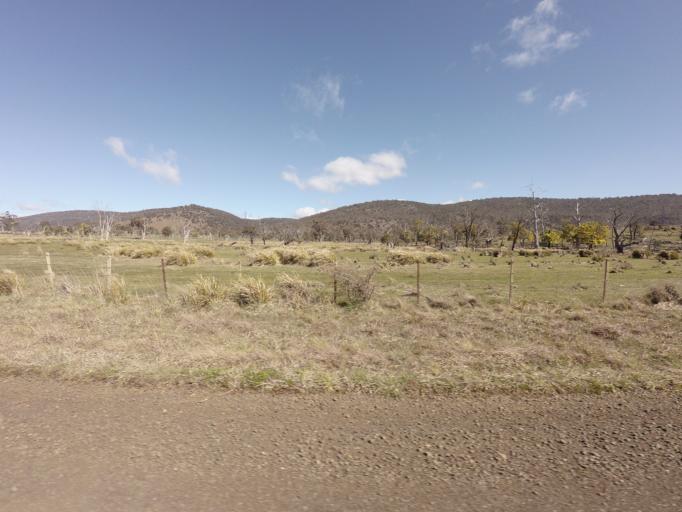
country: AU
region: Tasmania
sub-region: Northern Midlands
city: Evandale
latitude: -41.9426
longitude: 147.4275
